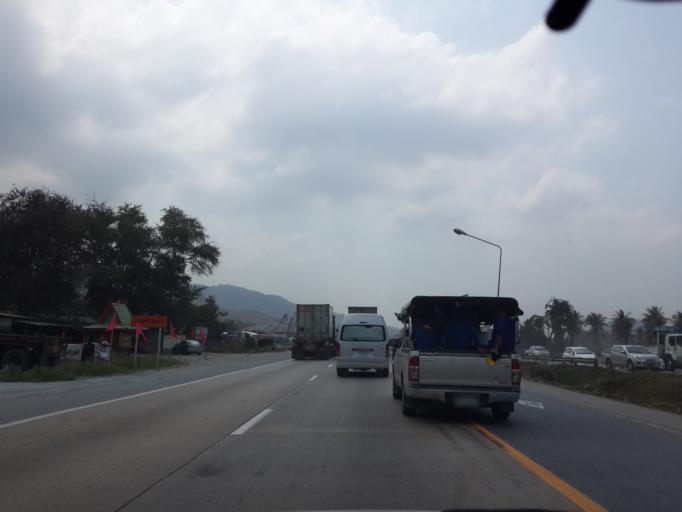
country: TH
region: Chon Buri
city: Chon Buri
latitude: 13.3121
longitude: 100.9927
